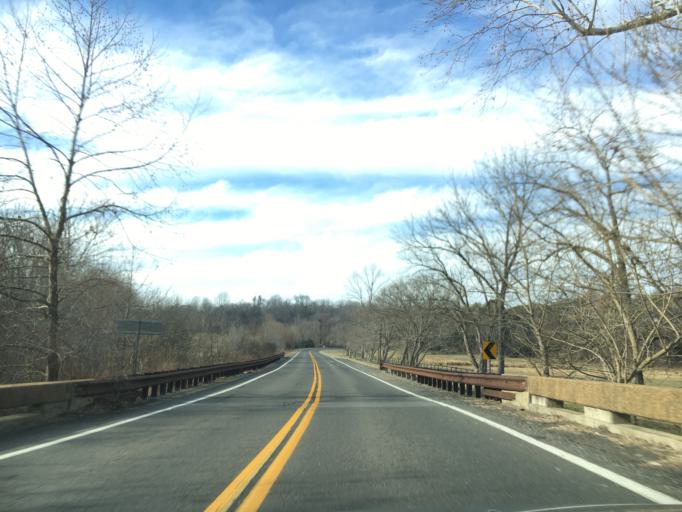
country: US
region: Virginia
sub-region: Fauquier County
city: Warrenton
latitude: 38.6993
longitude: -77.9071
